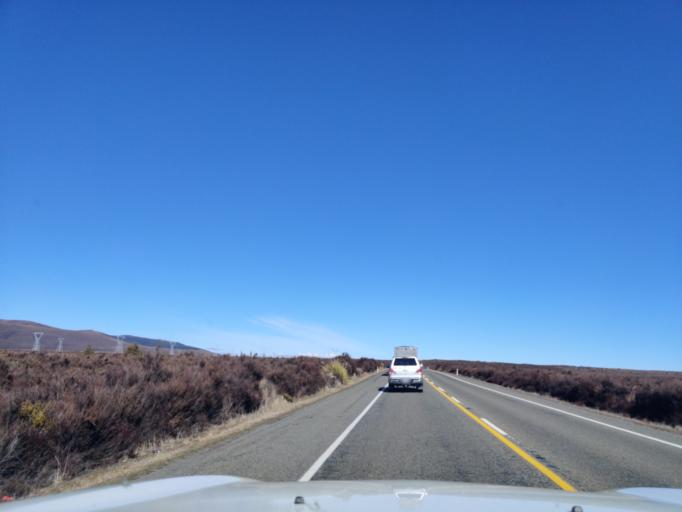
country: NZ
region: Manawatu-Wanganui
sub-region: Ruapehu District
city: Waiouru
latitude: -39.2544
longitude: 175.7358
